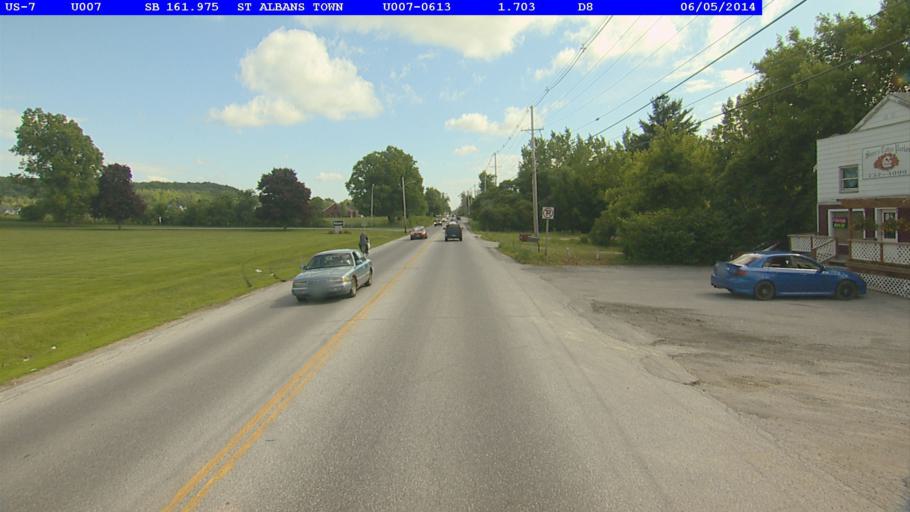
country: US
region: Vermont
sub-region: Franklin County
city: Saint Albans
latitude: 44.8332
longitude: -73.0792
